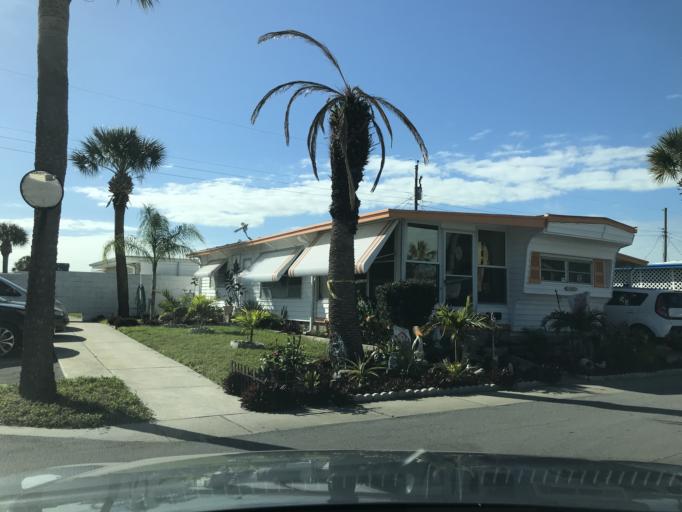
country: US
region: Florida
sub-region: Pinellas County
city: Belleair
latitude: 27.9298
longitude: -82.7906
